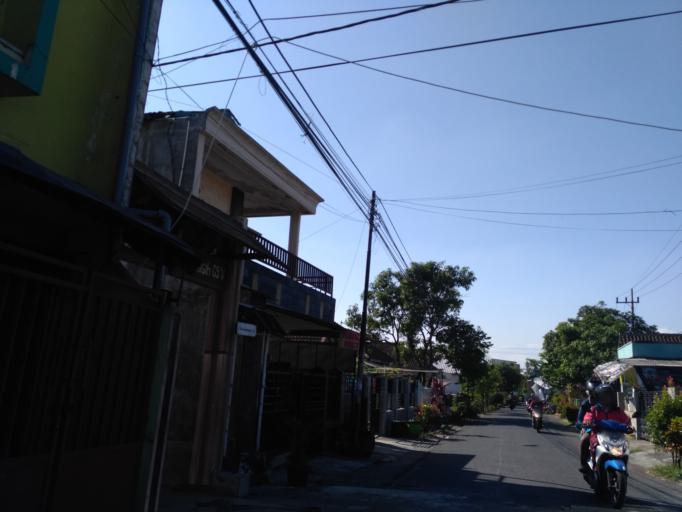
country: ID
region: East Java
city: Singosari
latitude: -7.9306
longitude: 112.6559
